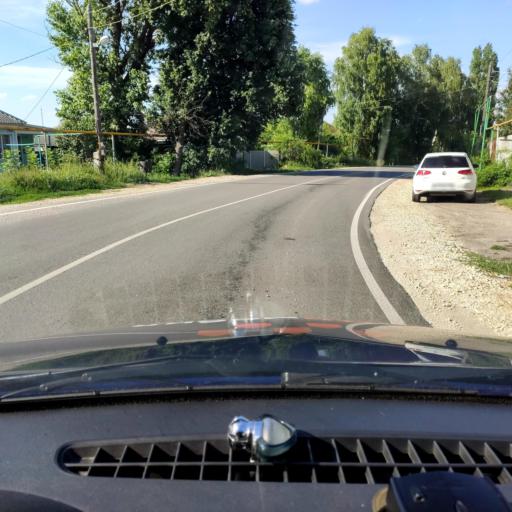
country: RU
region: Voronezj
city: Devitsa
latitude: 51.6565
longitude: 38.9704
